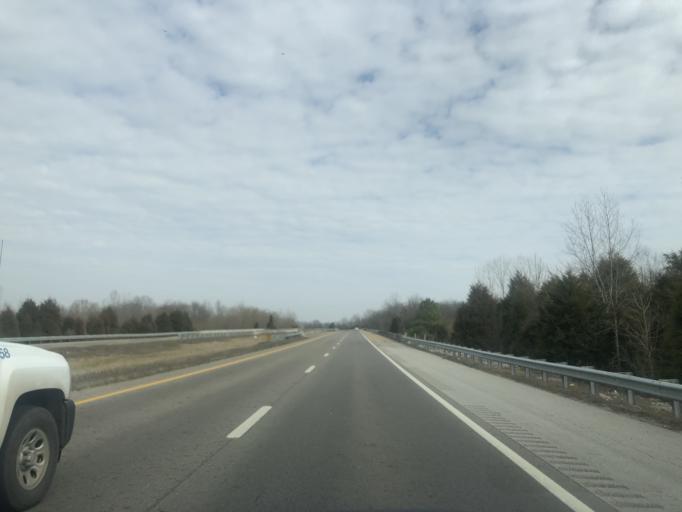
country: US
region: Tennessee
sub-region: Maury County
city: Mount Pleasant
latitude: 35.5878
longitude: -87.1291
